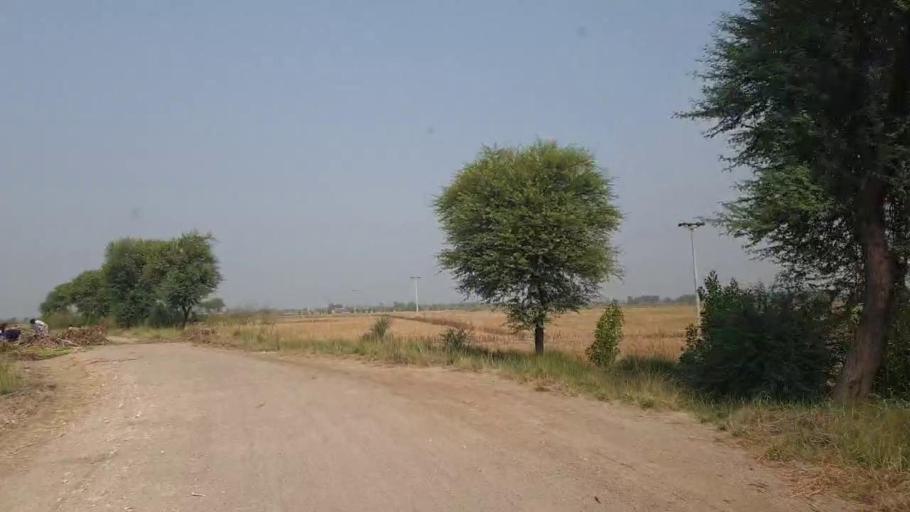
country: PK
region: Sindh
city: Matli
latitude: 25.1484
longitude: 68.7299
